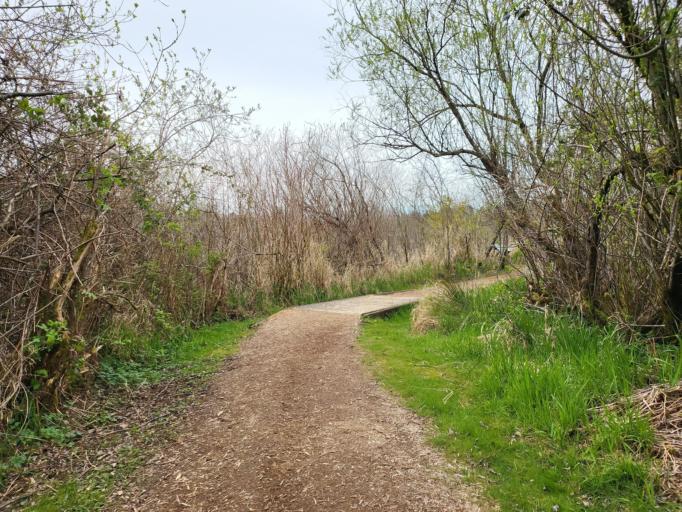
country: US
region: Washington
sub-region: King County
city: Newport
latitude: 47.5912
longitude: -122.1878
